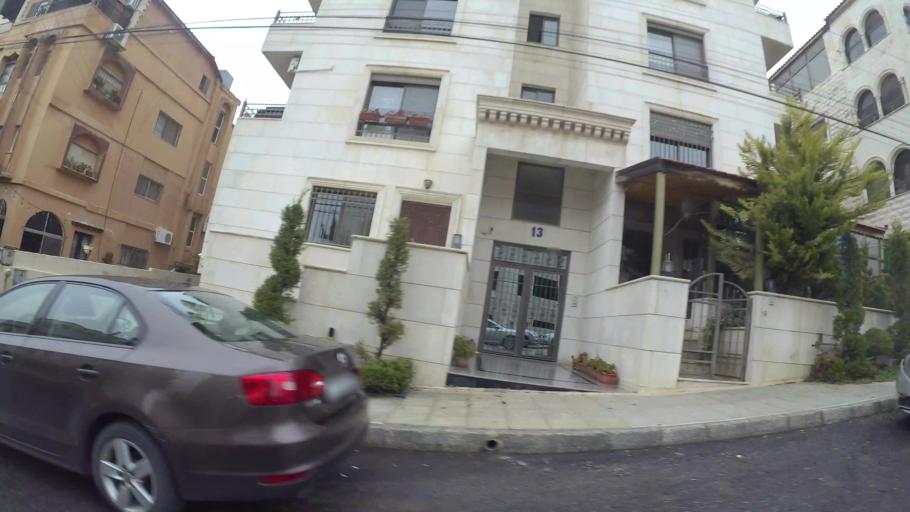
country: JO
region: Amman
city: Al Jubayhah
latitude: 32.0125
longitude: 35.8303
